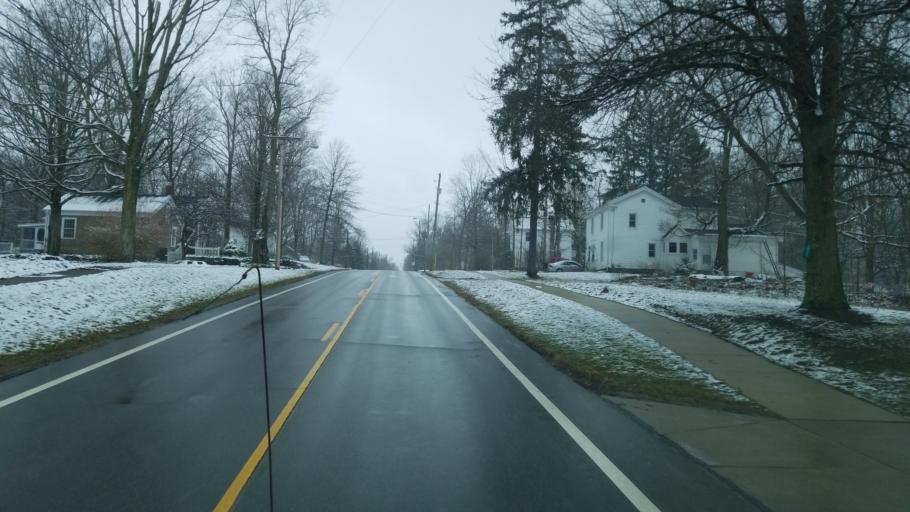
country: US
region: Ohio
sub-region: Portage County
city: Hiram
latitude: 41.3095
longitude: -81.1375
